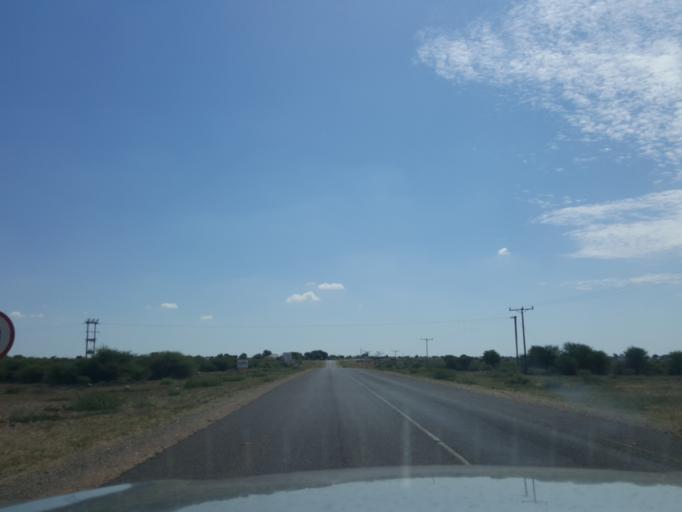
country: BW
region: Kweneng
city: Letlhakeng
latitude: -24.1175
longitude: 25.0487
